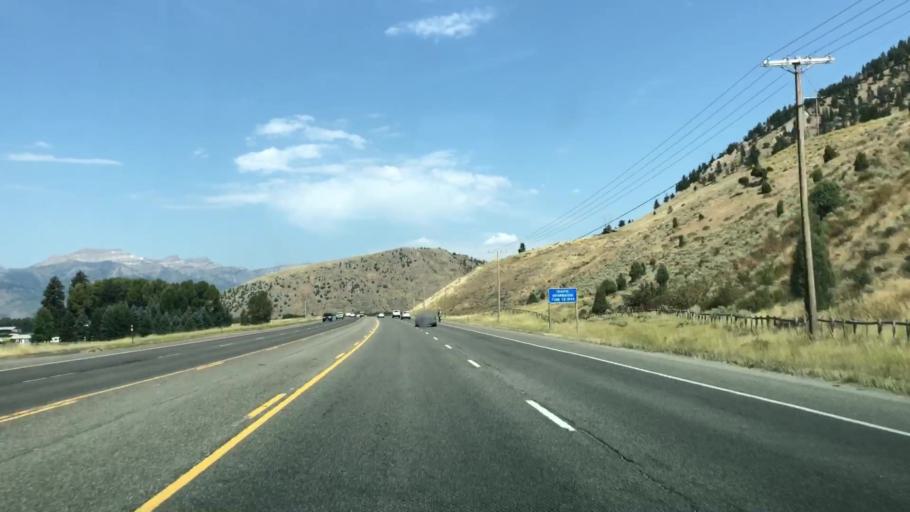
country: US
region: Wyoming
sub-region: Teton County
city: Rafter J Ranch
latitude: 43.4481
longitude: -110.7905
